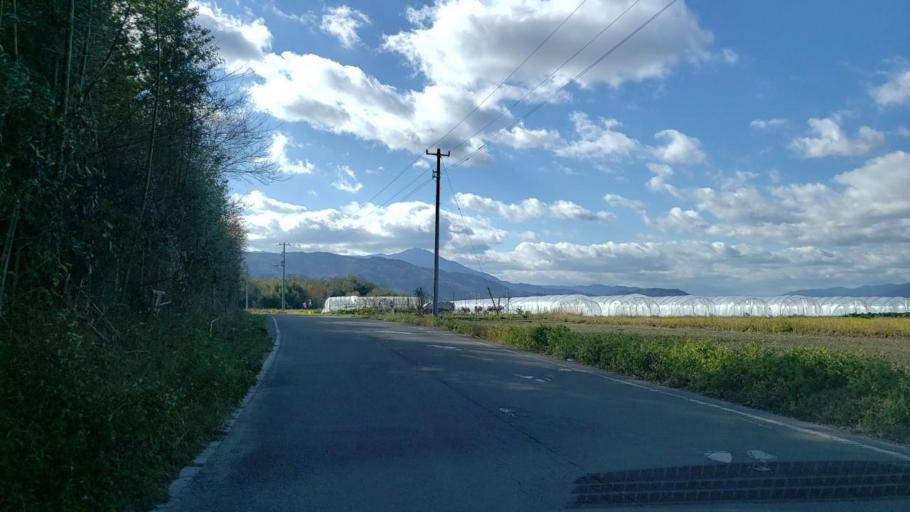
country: JP
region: Tokushima
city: Kamojimacho-jogejima
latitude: 34.0699
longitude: 134.3158
